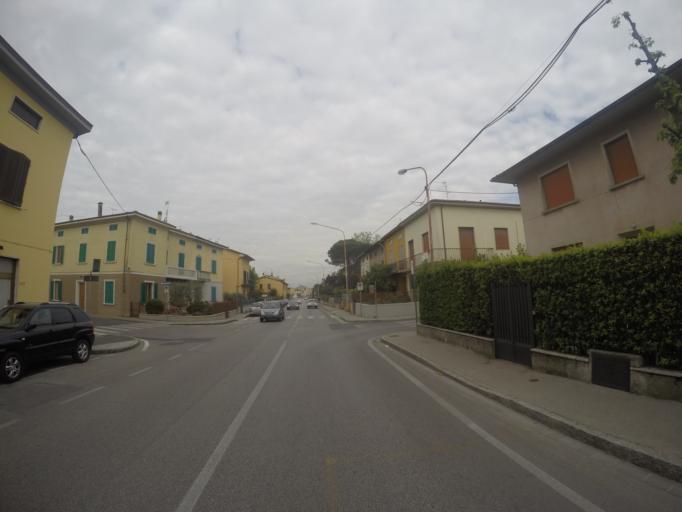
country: IT
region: Tuscany
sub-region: Provincia di Prato
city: Fornacelle
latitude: 43.8973
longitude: 11.0583
